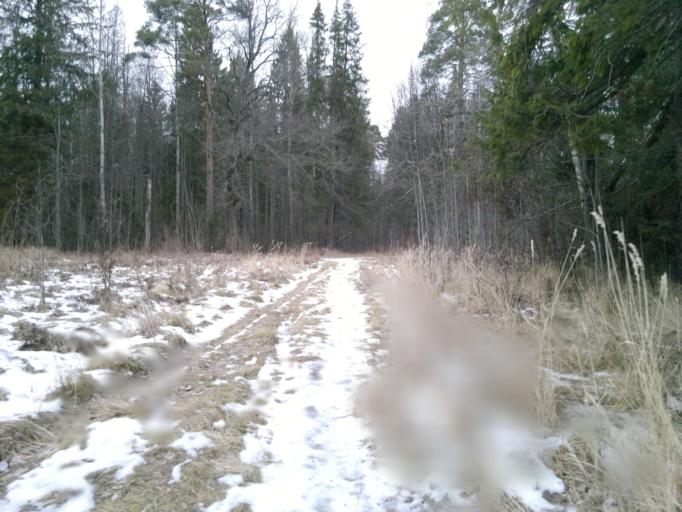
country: RU
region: Mariy-El
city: Yoshkar-Ola
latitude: 56.6106
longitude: 47.9479
